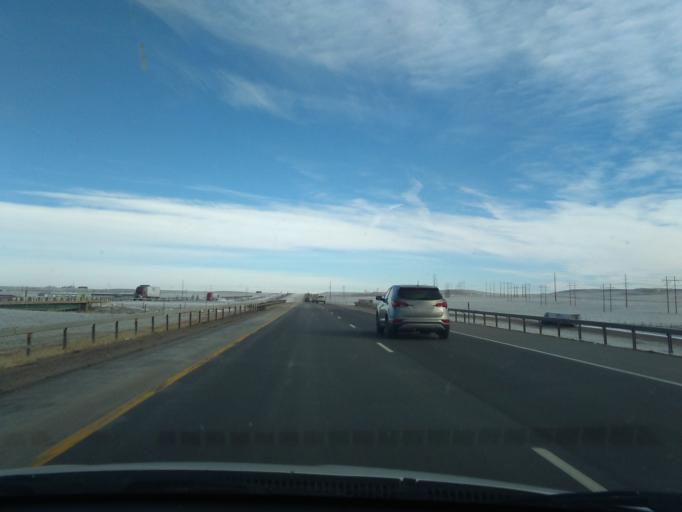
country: US
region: Wyoming
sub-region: Laramie County
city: Fox Farm-College
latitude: 41.1346
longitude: -104.7052
